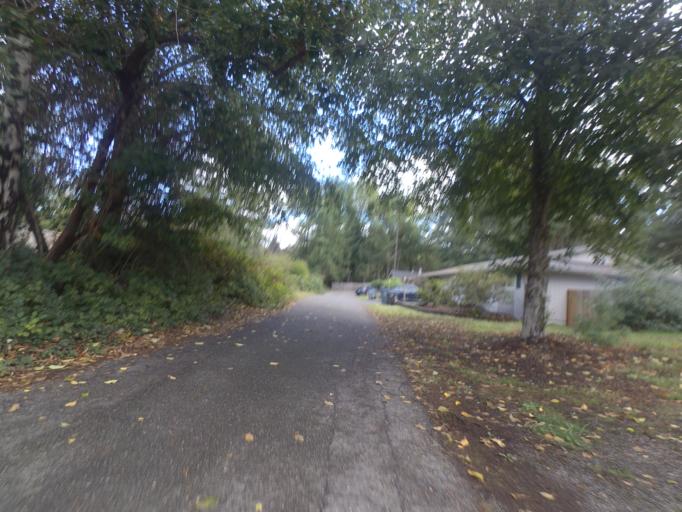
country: US
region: Washington
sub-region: Pierce County
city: University Place
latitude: 47.2238
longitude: -122.5434
